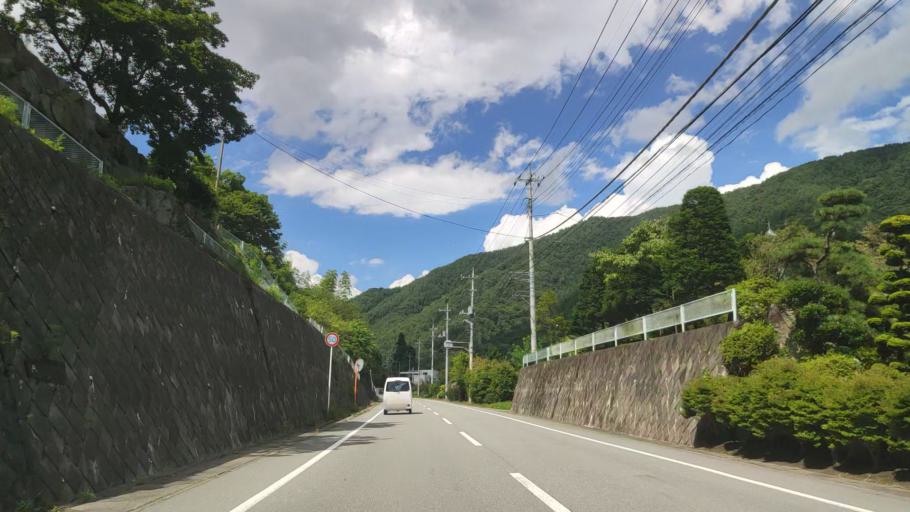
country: JP
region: Yamanashi
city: Enzan
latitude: 35.7720
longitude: 138.7378
